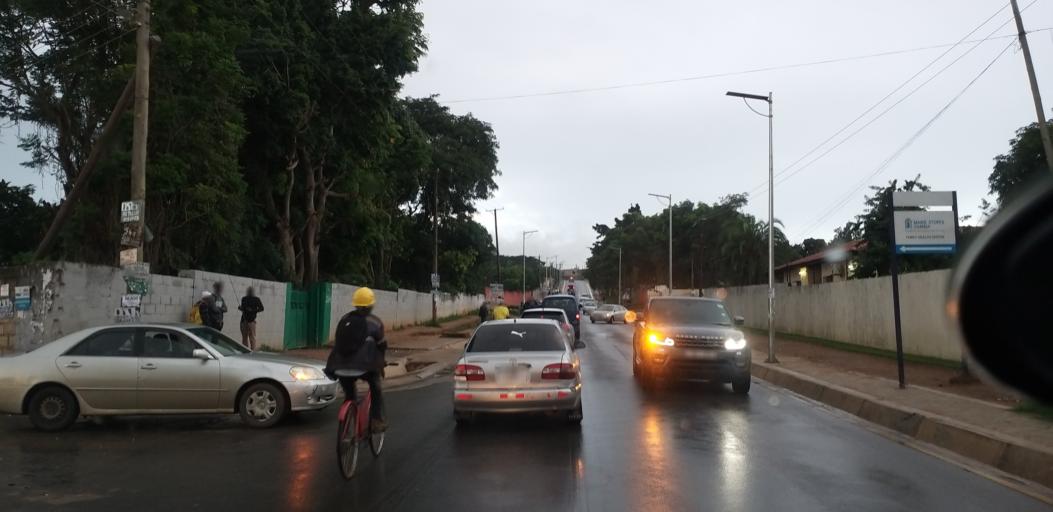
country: ZM
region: Lusaka
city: Lusaka
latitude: -15.4170
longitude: 28.3600
